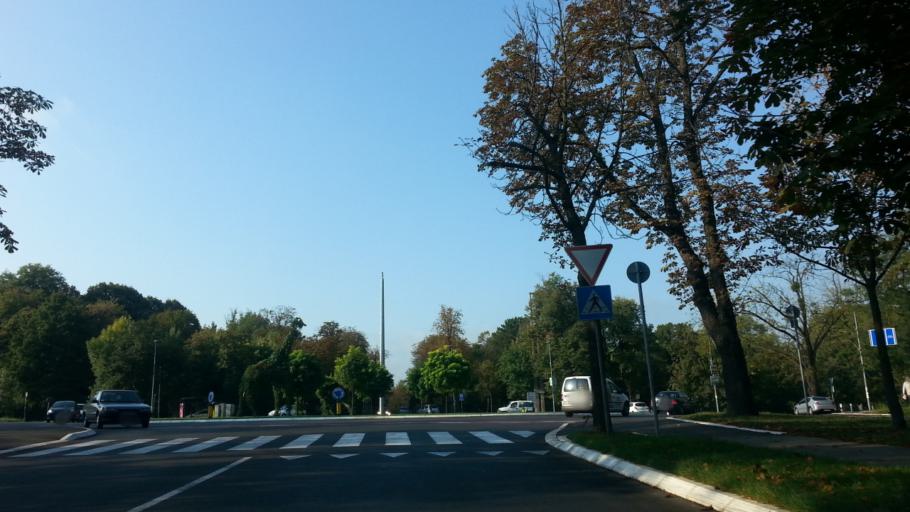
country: RS
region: Central Serbia
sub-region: Belgrade
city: Savski Venac
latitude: 44.7896
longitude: 20.4445
